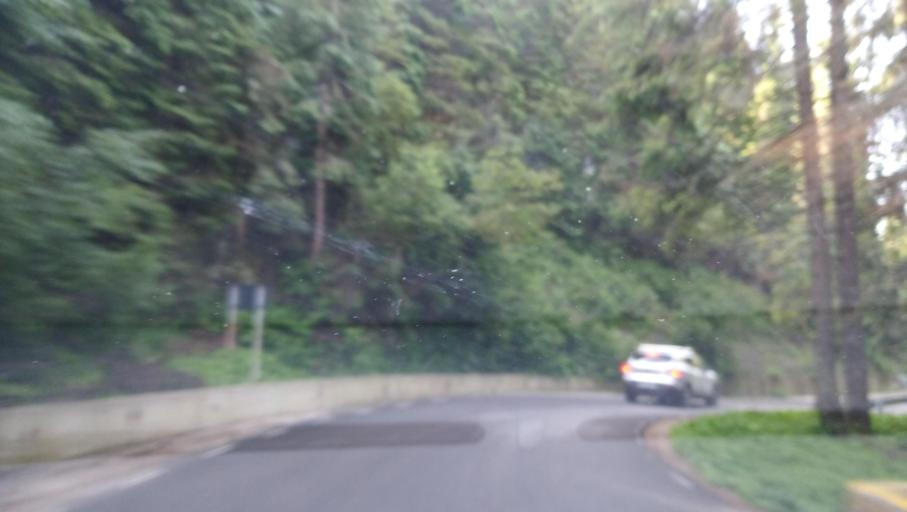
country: RO
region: Dambovita
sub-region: Comuna Moroeni
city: Glod
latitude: 45.3276
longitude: 25.4428
